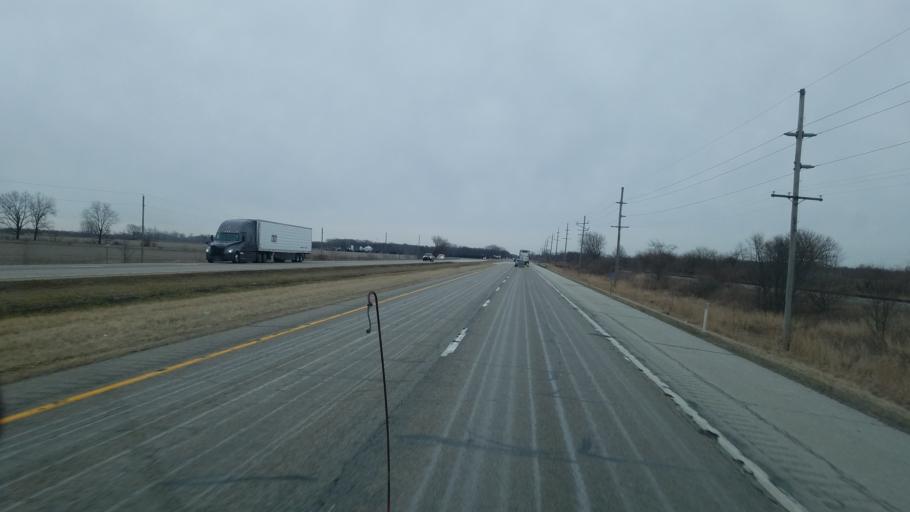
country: US
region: Indiana
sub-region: LaPorte County
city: Kingsford Heights
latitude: 41.4031
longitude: -86.7219
